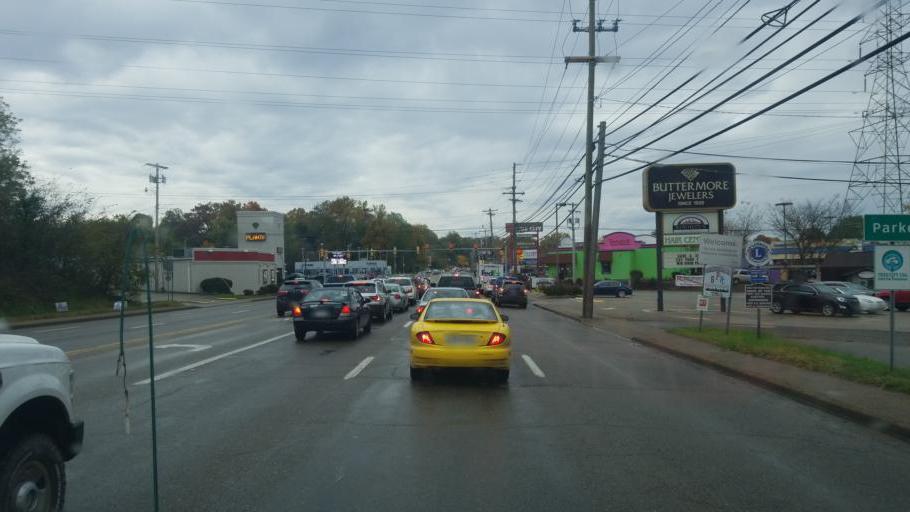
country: US
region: West Virginia
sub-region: Wood County
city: Vienna
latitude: 39.2961
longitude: -81.5468
